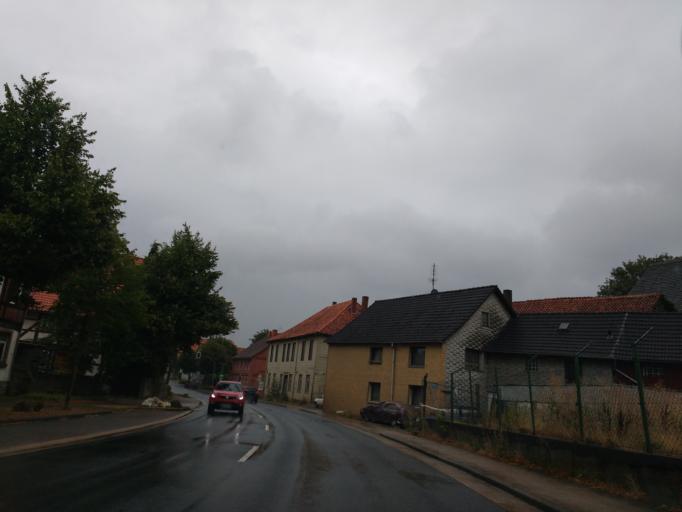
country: DE
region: Lower Saxony
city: Salzhemmendorf
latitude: 52.0839
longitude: 9.6016
